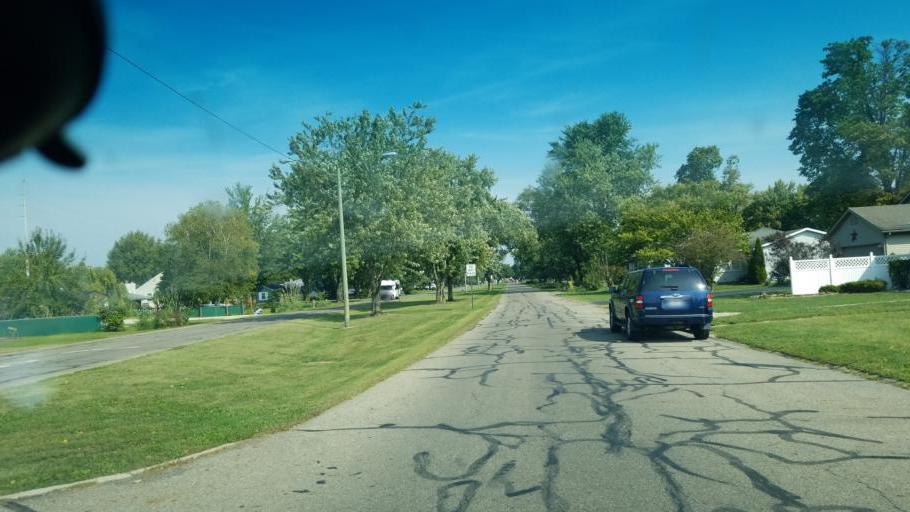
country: US
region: Ohio
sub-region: Marion County
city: Marion
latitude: 40.5810
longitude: -83.1063
